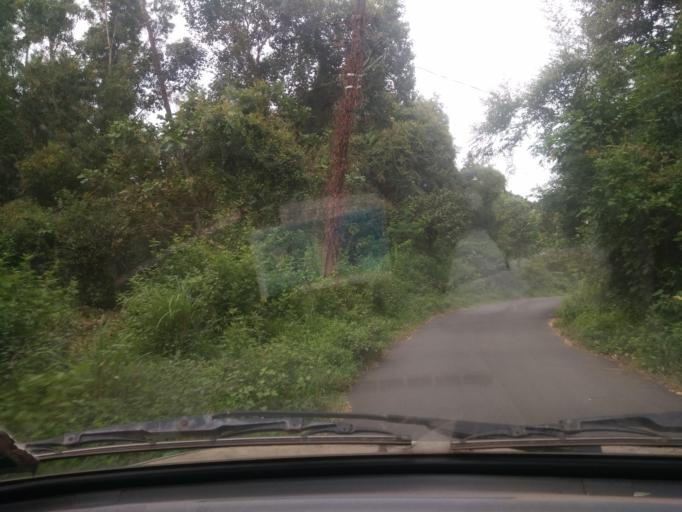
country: IN
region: Goa
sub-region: South Goa
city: Varca
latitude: 15.2203
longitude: 73.9494
